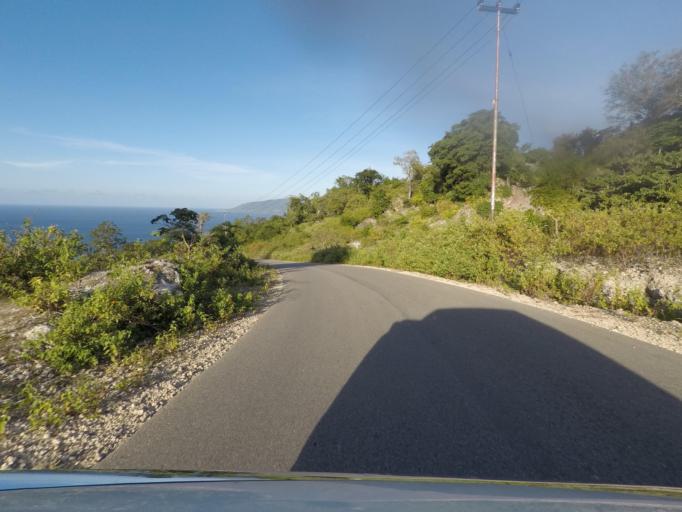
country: TL
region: Lautem
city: Lospalos
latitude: -8.3648
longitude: 127.0469
